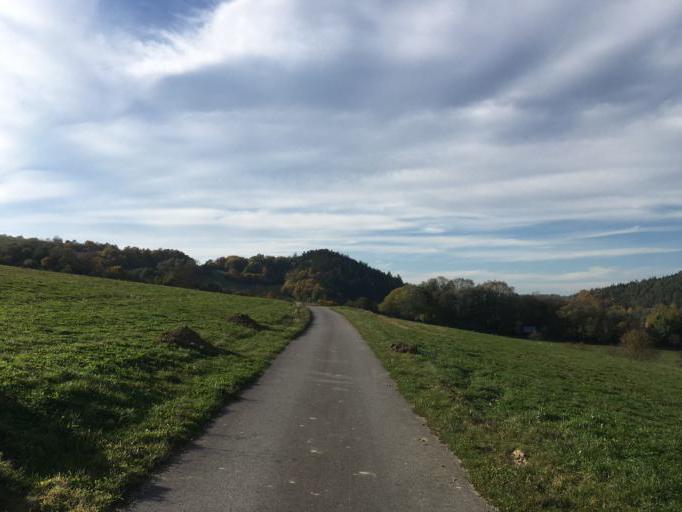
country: SK
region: Trenciansky
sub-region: Okres Povazska Bystrica
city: Povazska Bystrica
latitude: 49.0543
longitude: 18.4006
